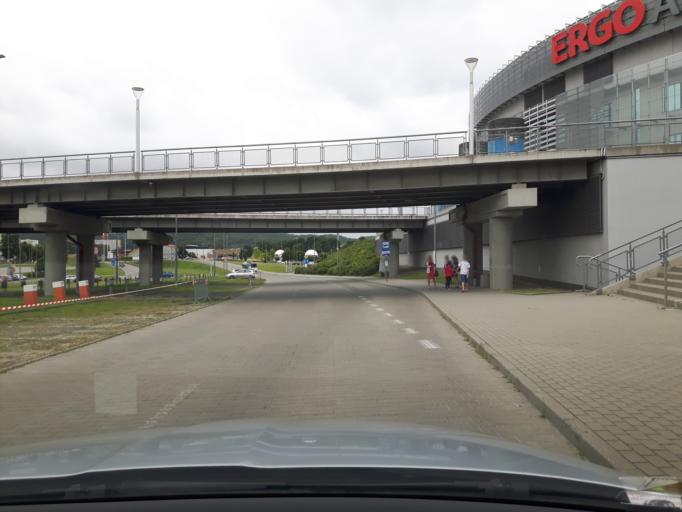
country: PL
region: Pomeranian Voivodeship
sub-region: Sopot
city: Sopot
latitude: 54.4257
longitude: 18.5817
